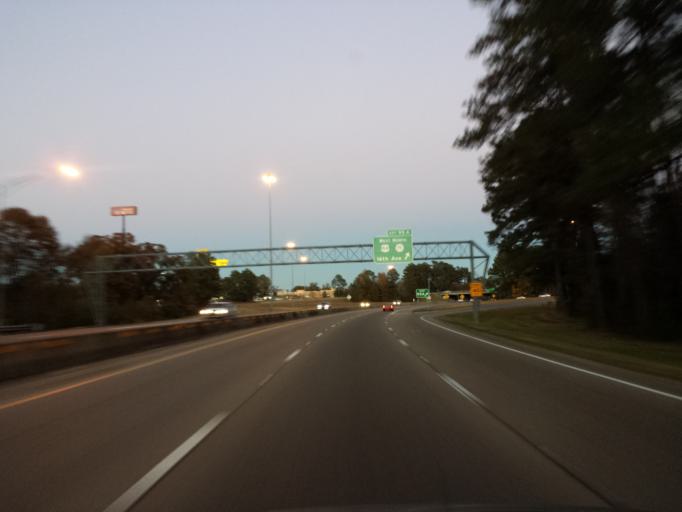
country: US
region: Mississippi
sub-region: Jones County
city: Laurel
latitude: 31.6829
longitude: -89.1507
